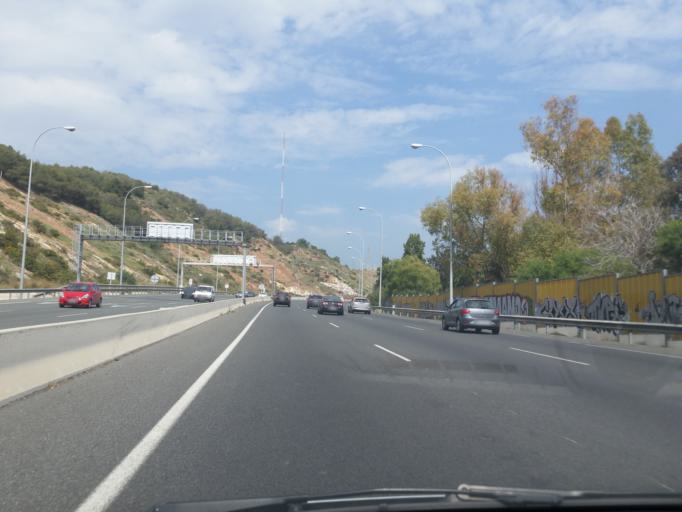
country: ES
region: Andalusia
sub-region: Provincia de Malaga
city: Malaga
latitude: 36.7280
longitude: -4.4538
